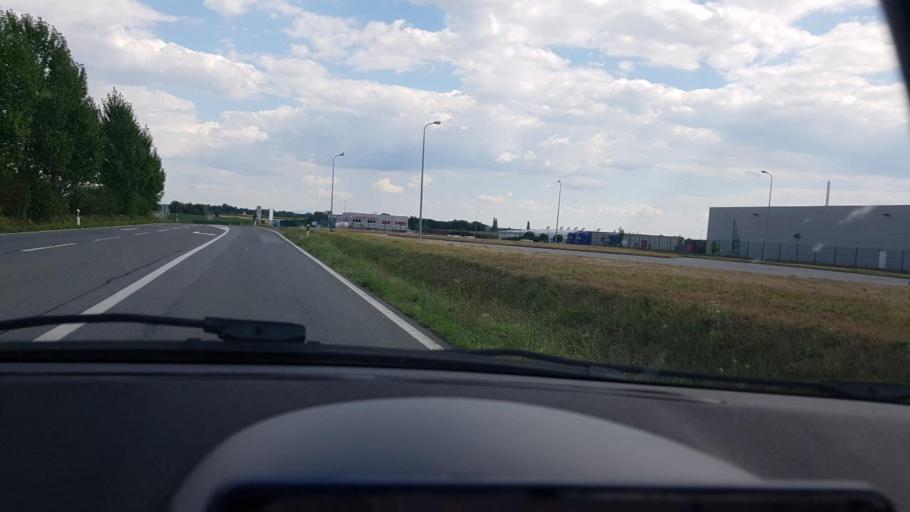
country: HR
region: Bjelovarsko-Bilogorska
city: Zdralovi
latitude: 45.8446
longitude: 16.9469
